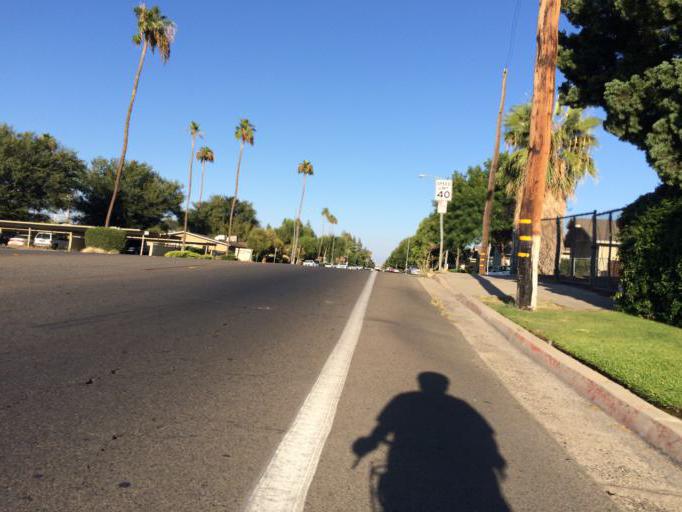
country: US
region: California
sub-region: Fresno County
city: Clovis
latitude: 36.8157
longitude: -119.7185
